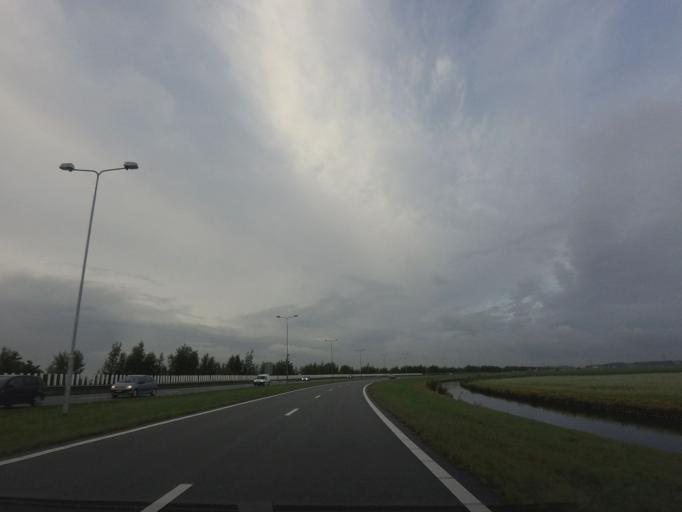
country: NL
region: North Holland
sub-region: Gemeente Haarlemmermeer
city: Hoofddorp
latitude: 52.3601
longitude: 4.7080
